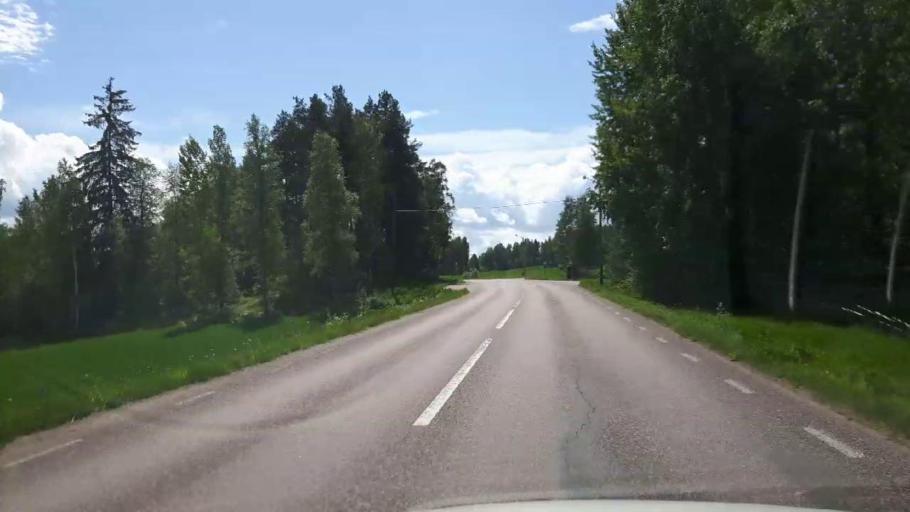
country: SE
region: Dalarna
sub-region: Faluns Kommun
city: Falun
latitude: 60.6300
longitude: 15.7677
